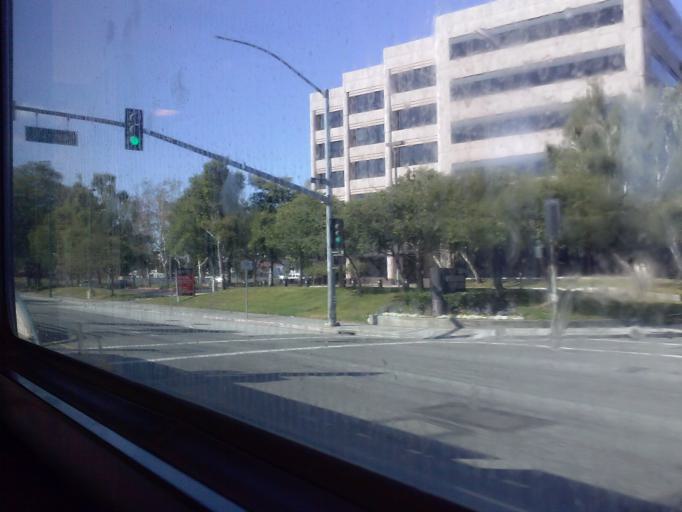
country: US
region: California
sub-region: Santa Clara County
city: Santa Clara
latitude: 37.3756
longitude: -121.9201
